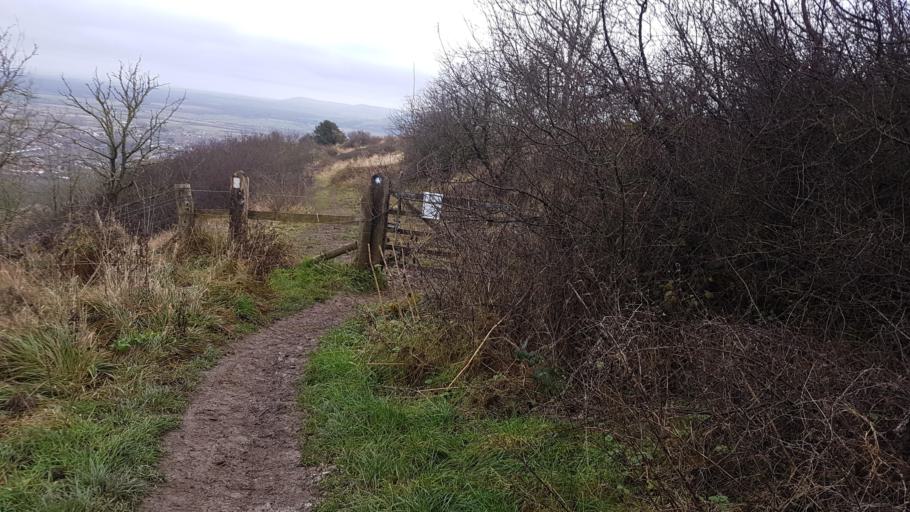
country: GB
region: England
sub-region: West Sussex
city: Steyning
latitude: 50.8806
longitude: -0.3478
